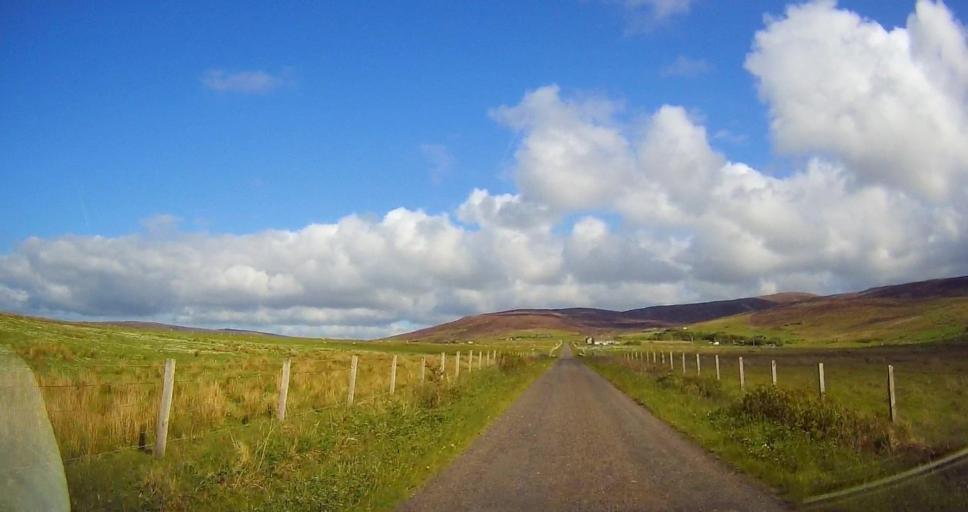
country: GB
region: Scotland
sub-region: Orkney Islands
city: Stromness
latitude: 58.9817
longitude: -3.1806
